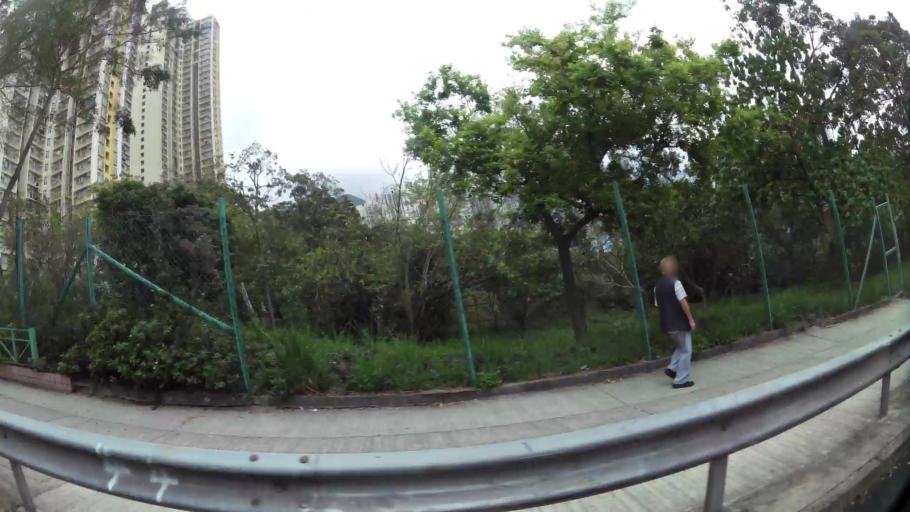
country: HK
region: Wong Tai Sin
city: Wong Tai Sin
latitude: 22.3486
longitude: 114.1949
